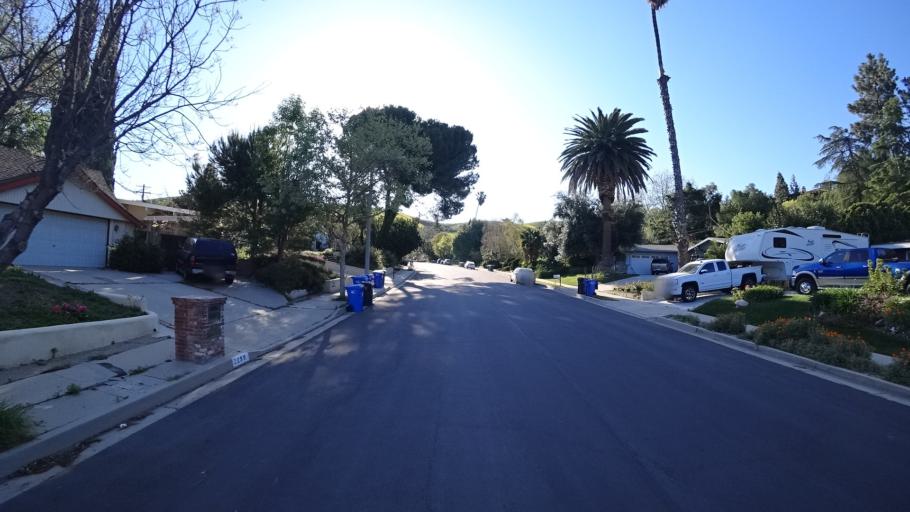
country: US
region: California
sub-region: Ventura County
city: Thousand Oaks
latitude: 34.1892
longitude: -118.8394
